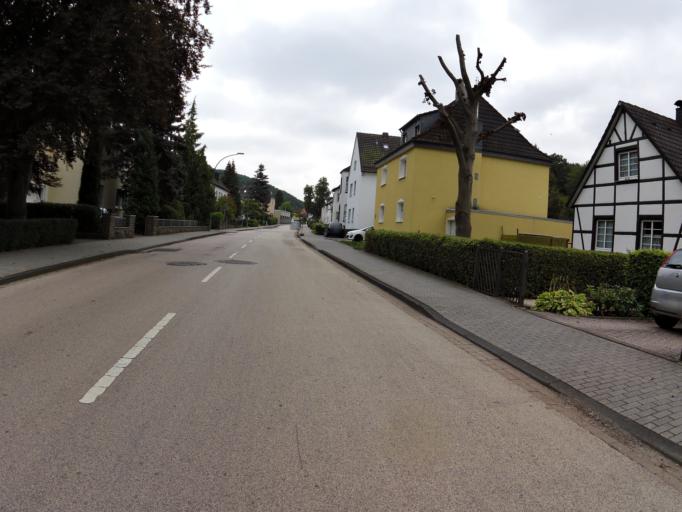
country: DE
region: North Rhine-Westphalia
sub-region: Regierungsbezirk Koln
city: Schleiden
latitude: 50.5759
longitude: 6.4923
